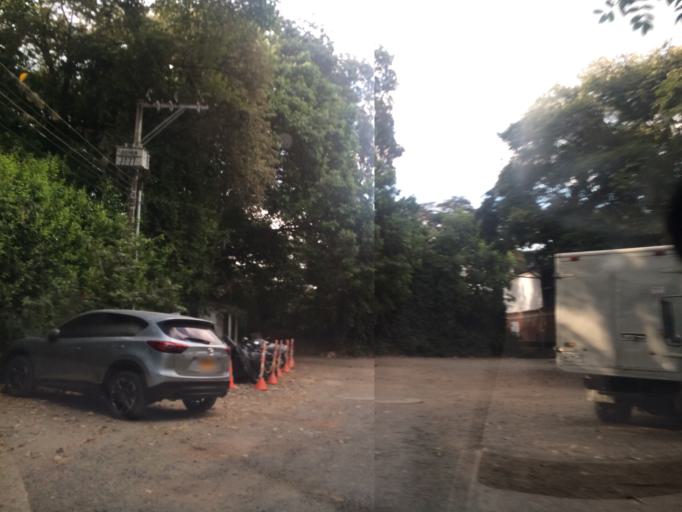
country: CO
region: Valle del Cauca
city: Cali
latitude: 3.3961
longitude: -76.5552
